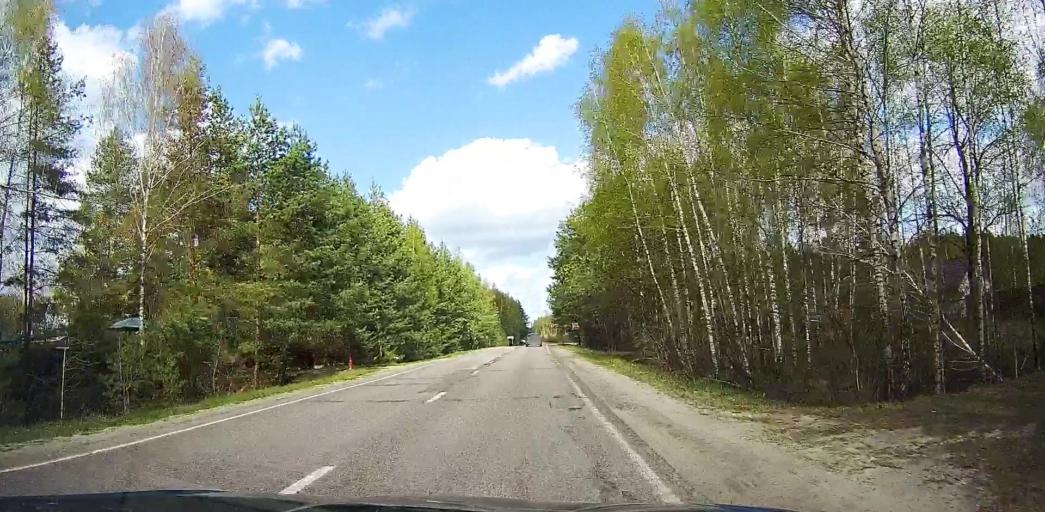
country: RU
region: Moskovskaya
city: Davydovo
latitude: 55.5904
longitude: 38.8323
